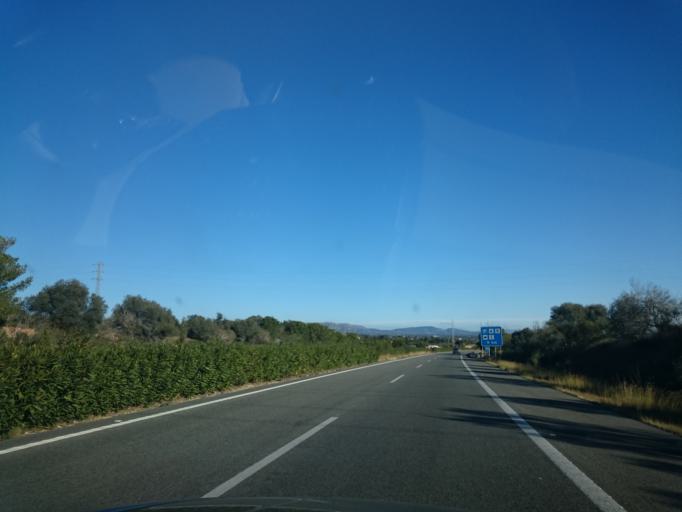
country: ES
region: Catalonia
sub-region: Provincia de Tarragona
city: Masdenverge
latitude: 40.7112
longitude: 0.5545
